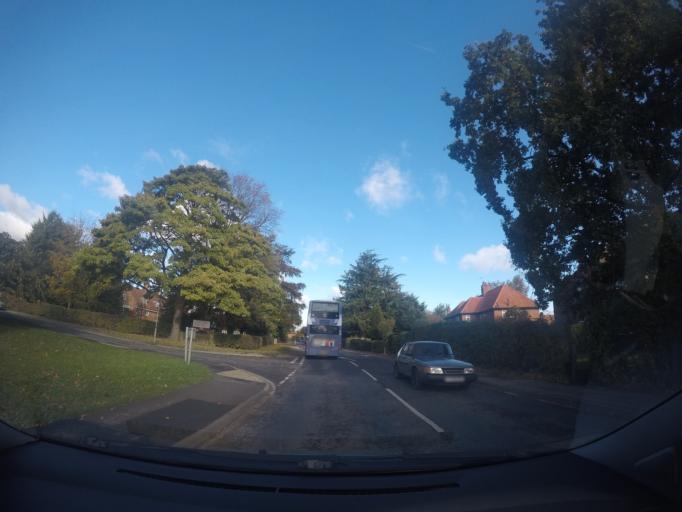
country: GB
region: England
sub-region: City of York
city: Haxby
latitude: 53.9919
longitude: -1.0725
